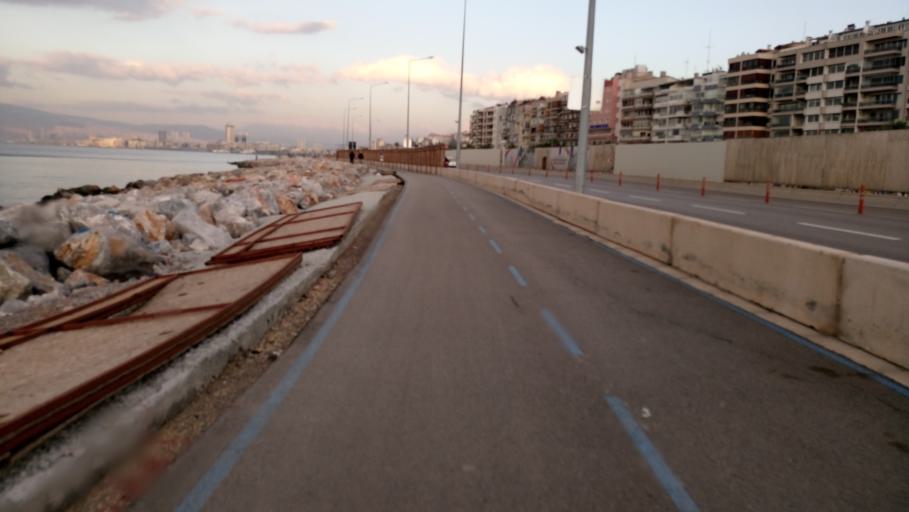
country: TR
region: Izmir
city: Izmir
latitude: 38.4086
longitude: 27.1073
